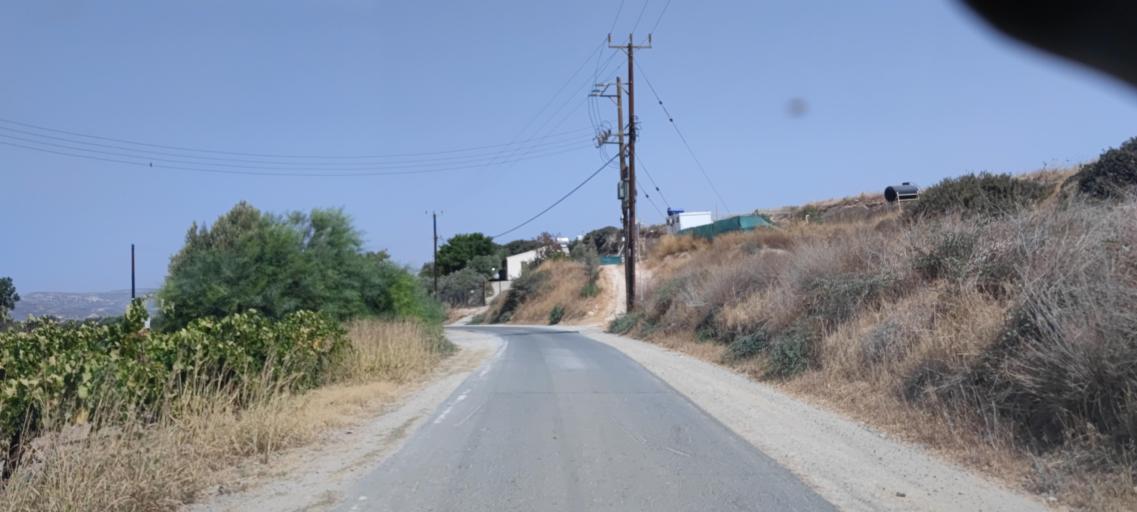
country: CY
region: Limassol
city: Pissouri
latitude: 34.6657
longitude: 32.7675
